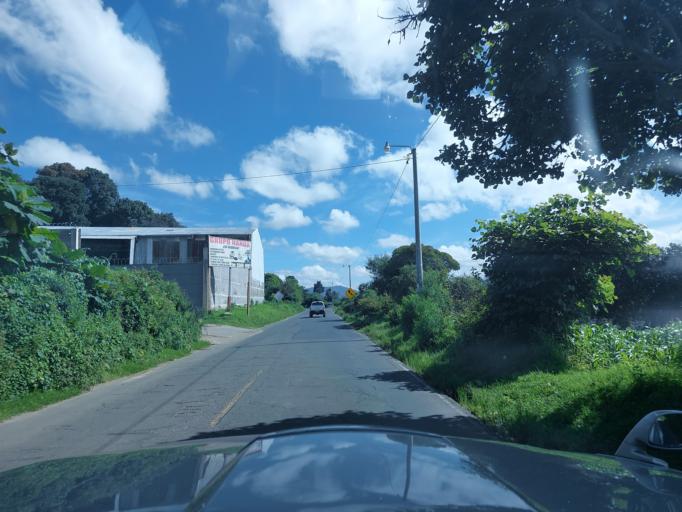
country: GT
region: Chimaltenango
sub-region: Municipio de Zaragoza
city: Zaragoza
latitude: 14.6559
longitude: -90.8970
